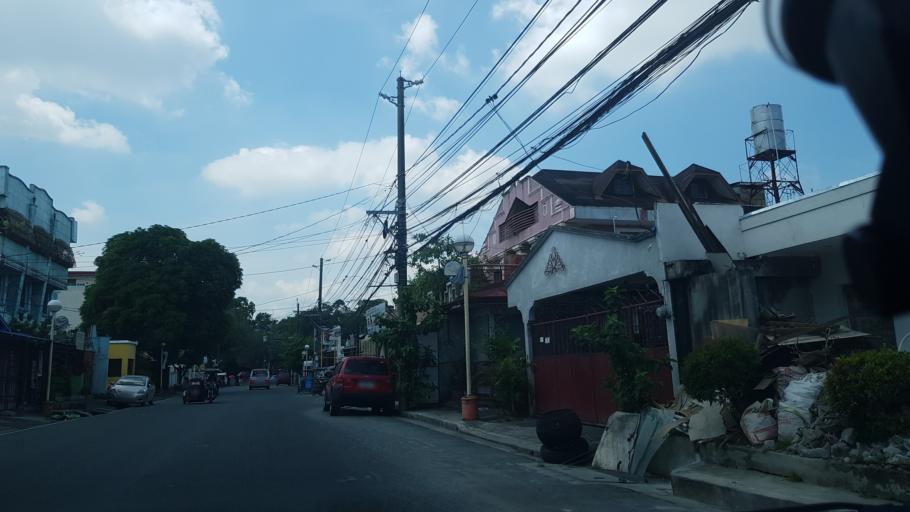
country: PH
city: Sambayanihan People's Village
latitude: 14.4275
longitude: 120.9996
